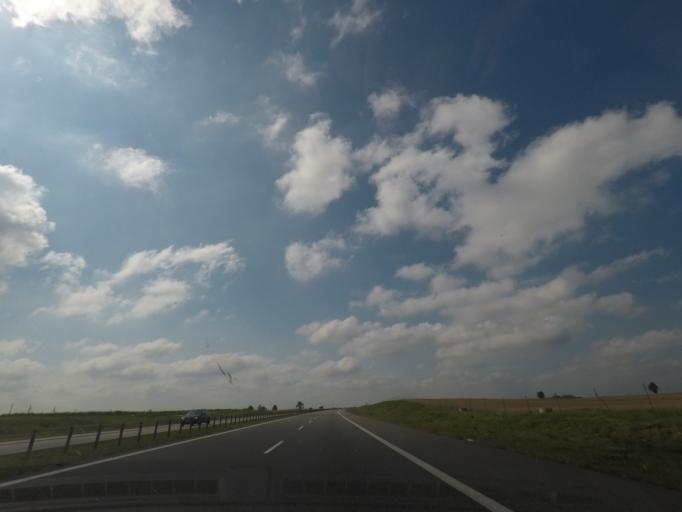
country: PL
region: Kujawsko-Pomorskie
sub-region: Powiat wabrzeski
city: Pluznica
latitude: 53.1985
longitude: 18.7398
